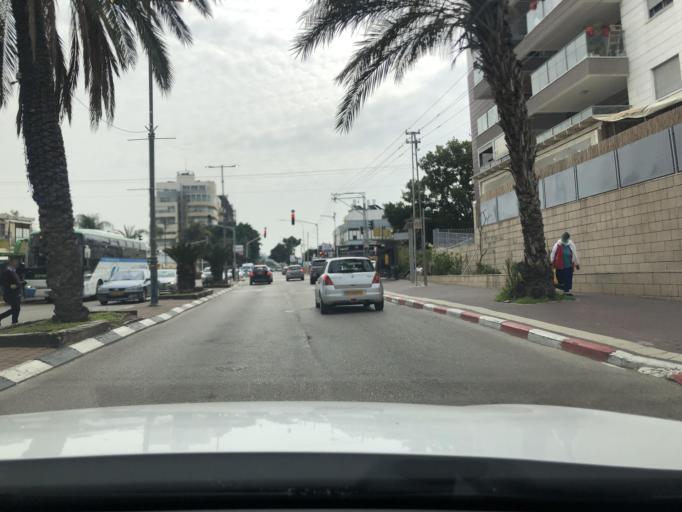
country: IL
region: Central District
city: Rosh Ha'Ayin
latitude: 32.0959
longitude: 34.9441
